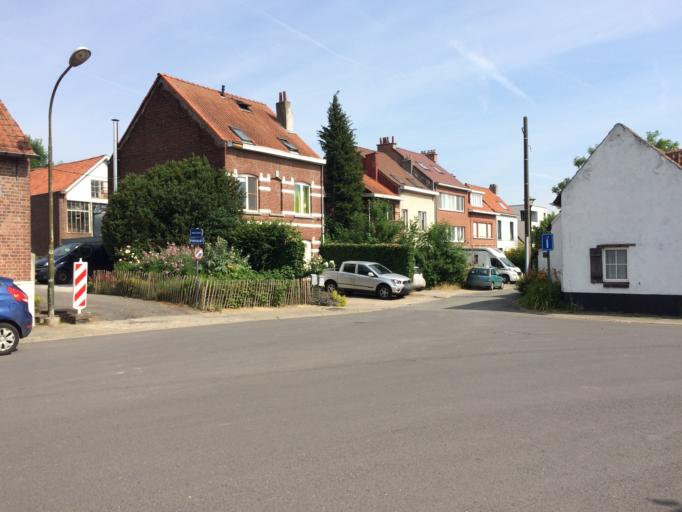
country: BE
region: Flanders
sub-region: Provincie Vlaams-Brabant
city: Bever
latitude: 50.9086
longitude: 4.3146
